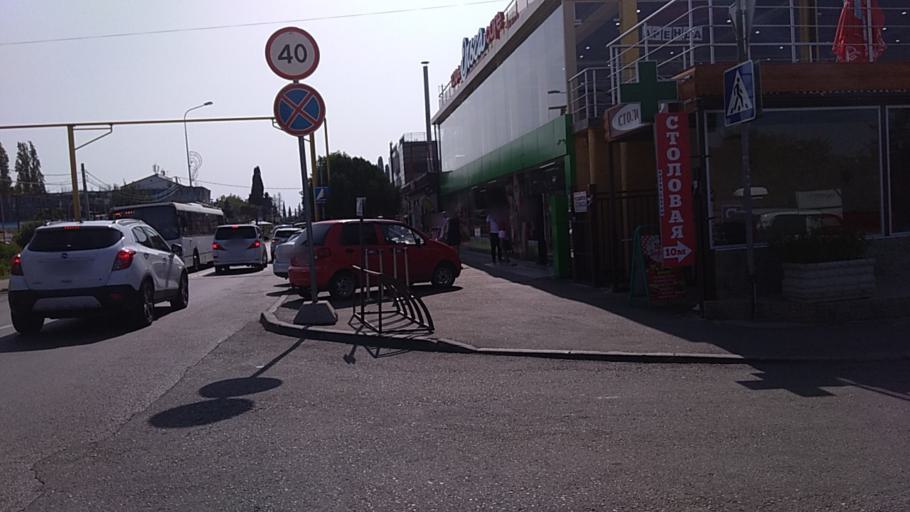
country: RU
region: Krasnodarskiy
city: Adler
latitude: 43.3925
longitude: 39.9871
